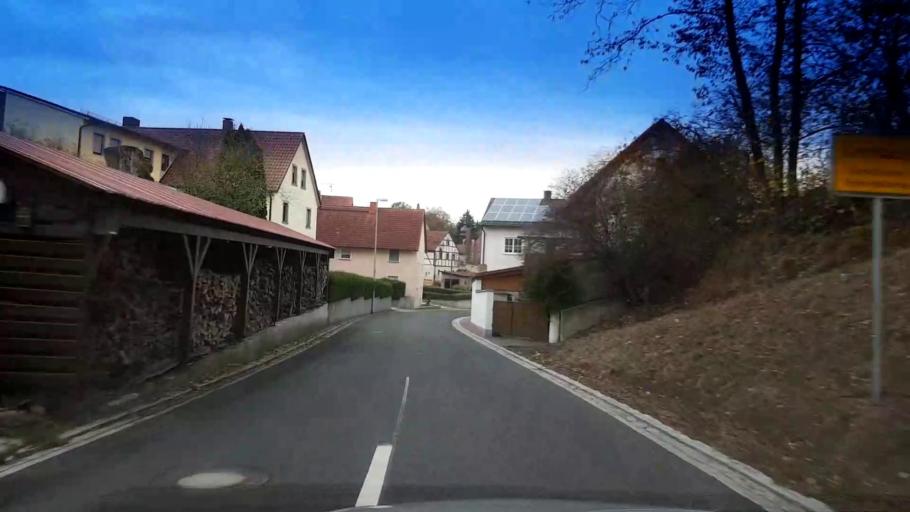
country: DE
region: Bavaria
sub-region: Upper Franconia
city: Priesendorf
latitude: 49.9295
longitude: 10.6960
